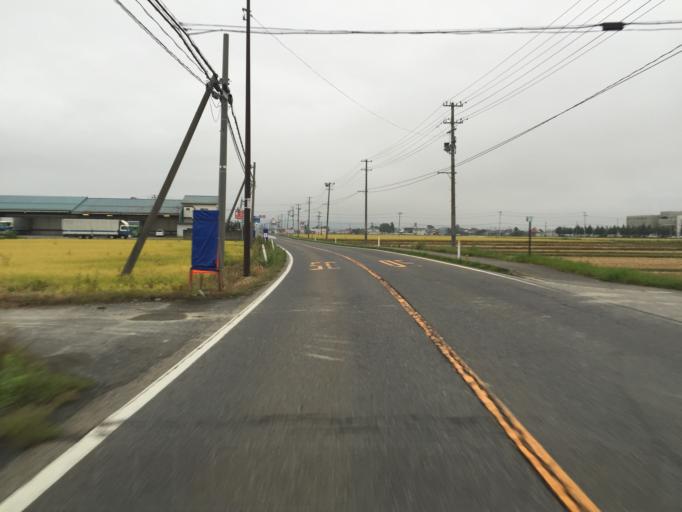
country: JP
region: Fukushima
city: Kitakata
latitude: 37.5282
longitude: 139.8870
